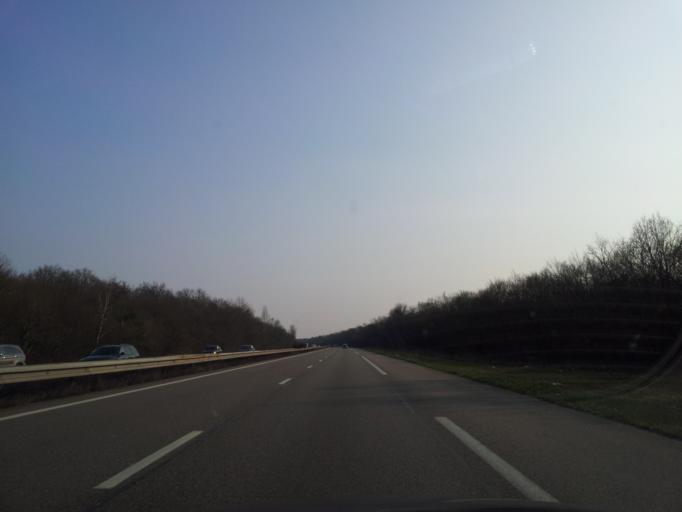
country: FR
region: Alsace
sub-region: Departement du Haut-Rhin
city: Habsheim
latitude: 47.7084
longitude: 7.4384
